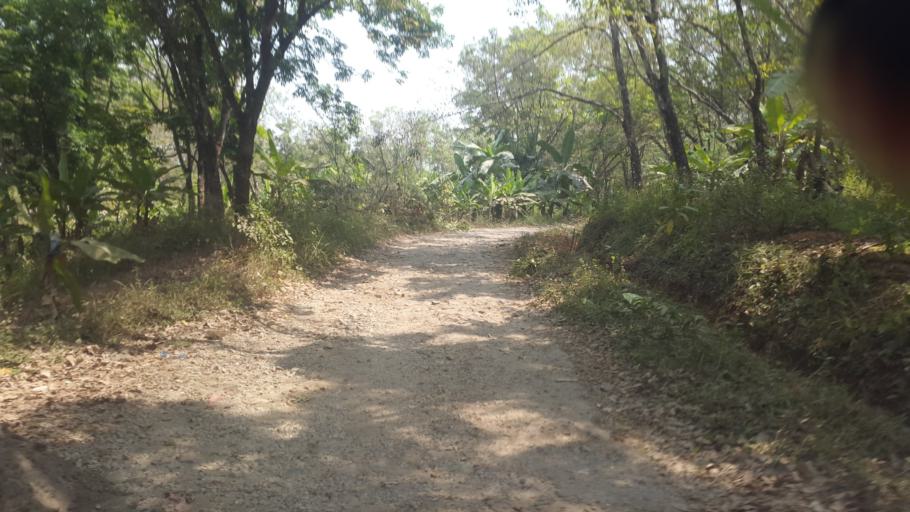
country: ID
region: West Java
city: Cimaja
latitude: -6.9396
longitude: 106.4998
